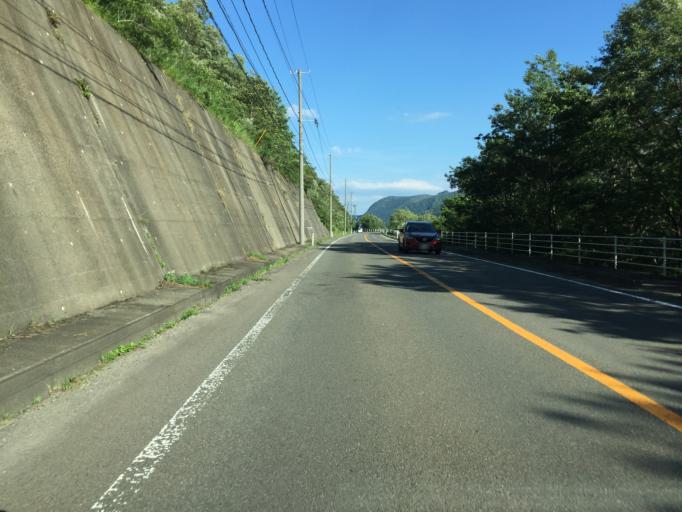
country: JP
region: Miyagi
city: Shiroishi
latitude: 37.9816
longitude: 140.4799
